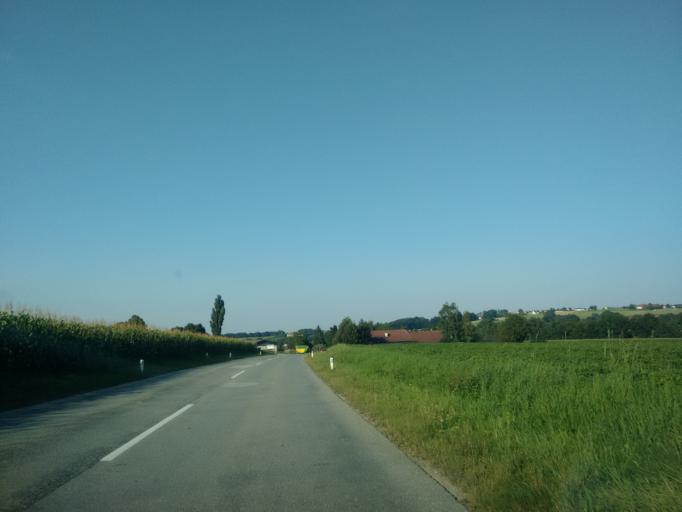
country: AT
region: Upper Austria
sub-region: Wels-Land
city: Sattledt
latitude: 48.0049
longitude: 14.0378
